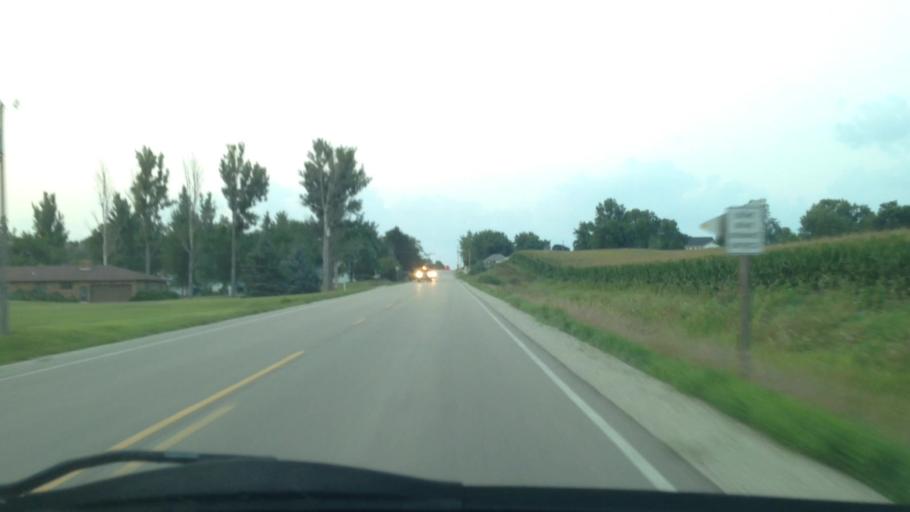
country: US
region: Iowa
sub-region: Benton County
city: Urbana
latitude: 42.2199
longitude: -91.8714
